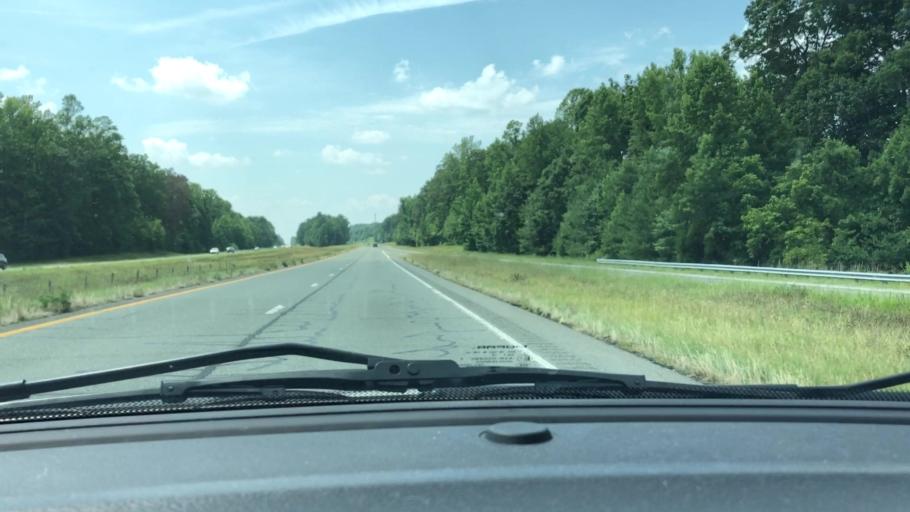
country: US
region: North Carolina
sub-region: Chatham County
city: Siler City
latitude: 35.7660
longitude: -79.4774
